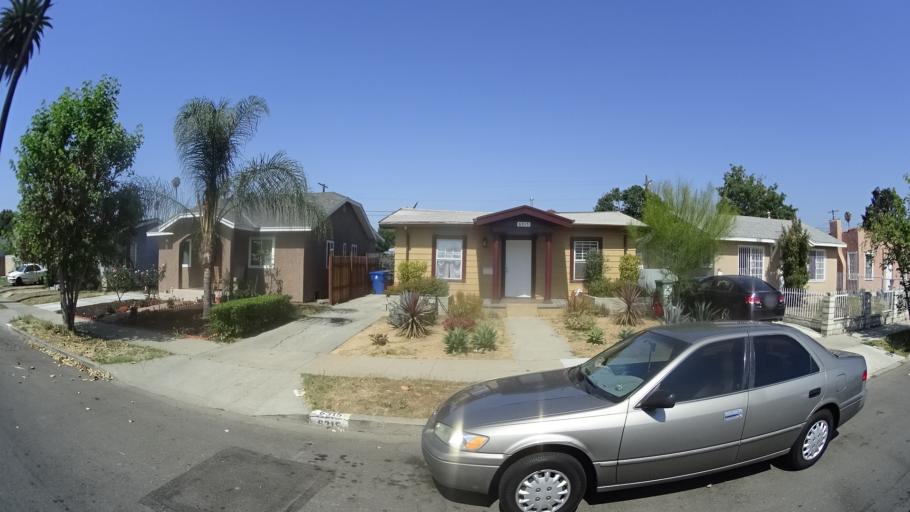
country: US
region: California
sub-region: Los Angeles County
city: View Park-Windsor Hills
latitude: 33.9825
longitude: -118.3246
